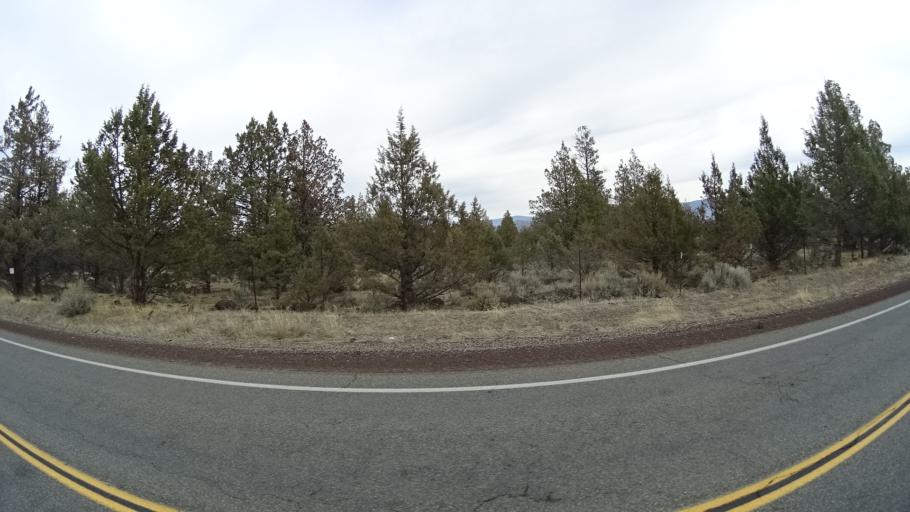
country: US
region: California
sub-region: Siskiyou County
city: Montague
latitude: 41.6359
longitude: -122.4544
